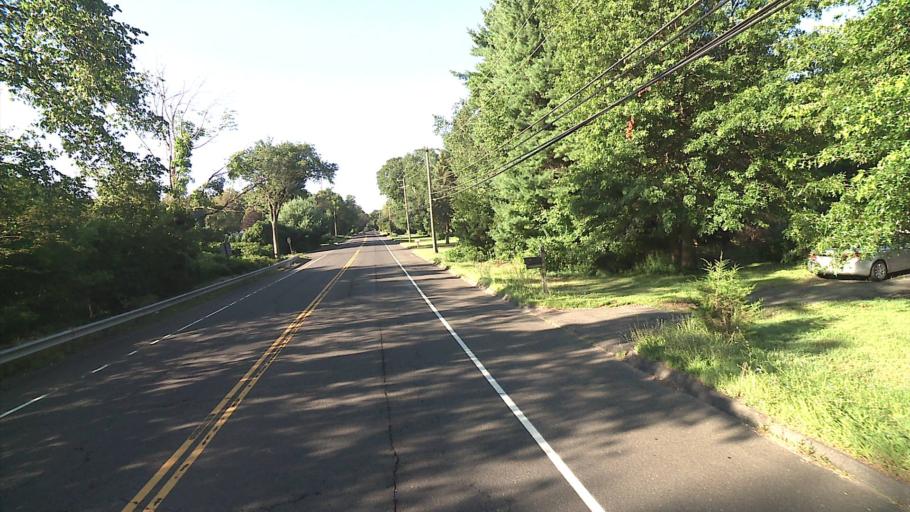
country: US
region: Connecticut
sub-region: New Haven County
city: Cheshire
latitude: 41.4602
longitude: -72.9079
